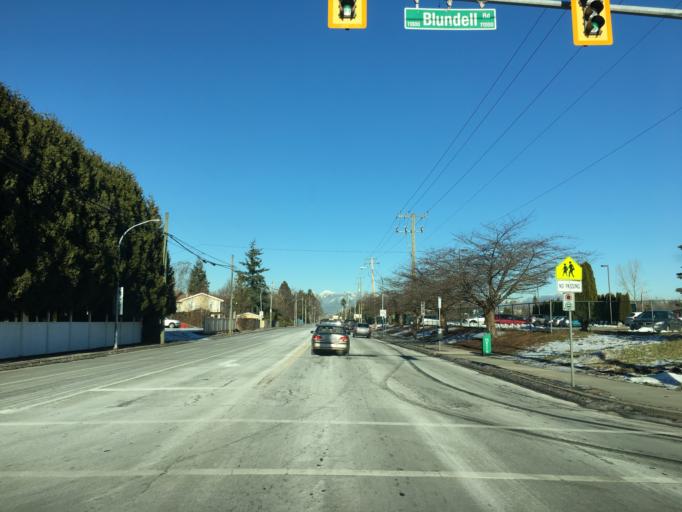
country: CA
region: British Columbia
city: Richmond
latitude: 49.1555
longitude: -123.0917
